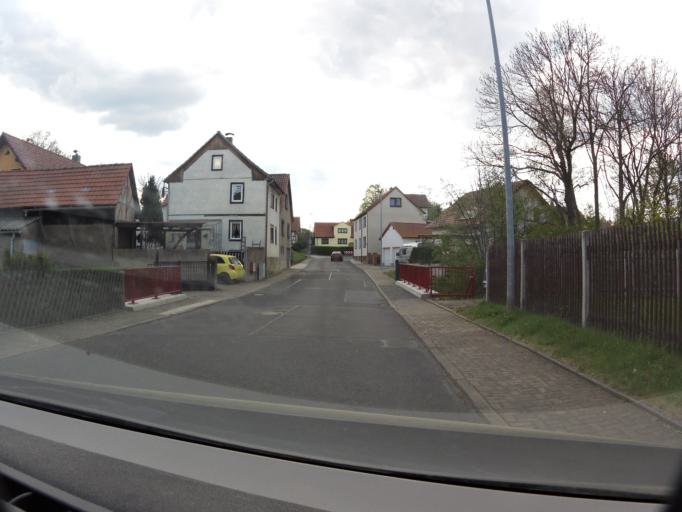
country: DE
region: Thuringia
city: Petriroda
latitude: 50.8678
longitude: 10.7017
